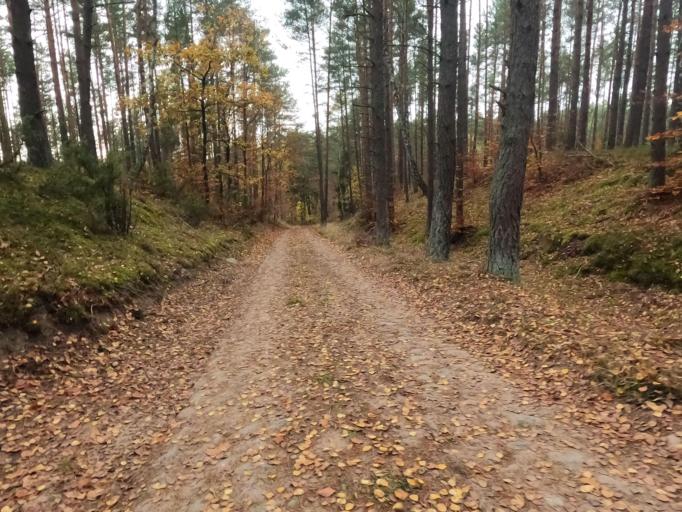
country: PL
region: Pomeranian Voivodeship
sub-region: Powiat starogardzki
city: Skarszewy
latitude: 54.0515
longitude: 18.4442
